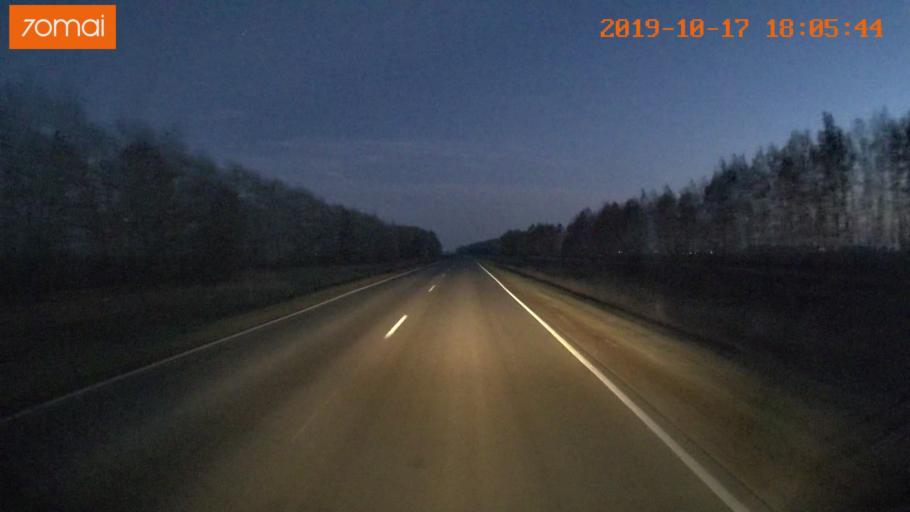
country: RU
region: Tula
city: Kurkino
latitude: 53.4621
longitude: 38.6473
